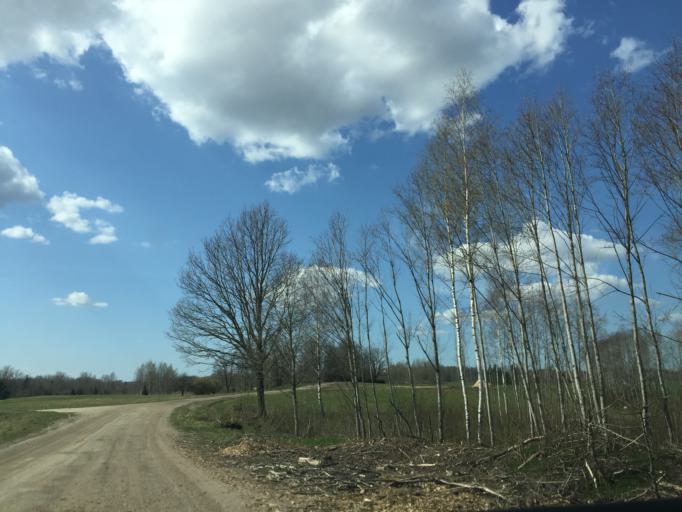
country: LV
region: Skriveri
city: Skriveri
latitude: 56.7928
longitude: 25.1558
